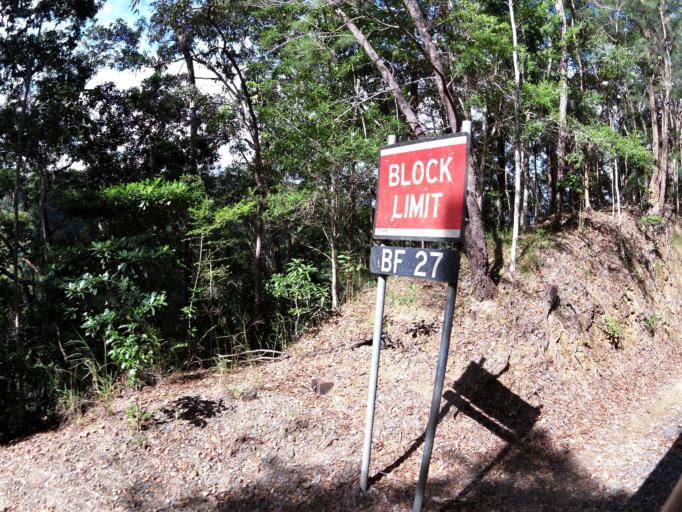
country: AU
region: Queensland
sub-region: Tablelands
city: Kuranda
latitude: -16.8340
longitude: 145.6424
